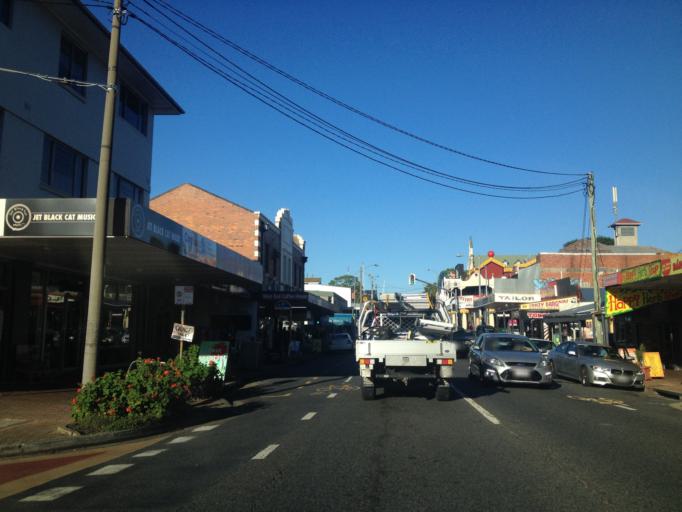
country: AU
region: Queensland
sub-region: Brisbane
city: South Brisbane
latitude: -27.4809
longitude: 153.0112
